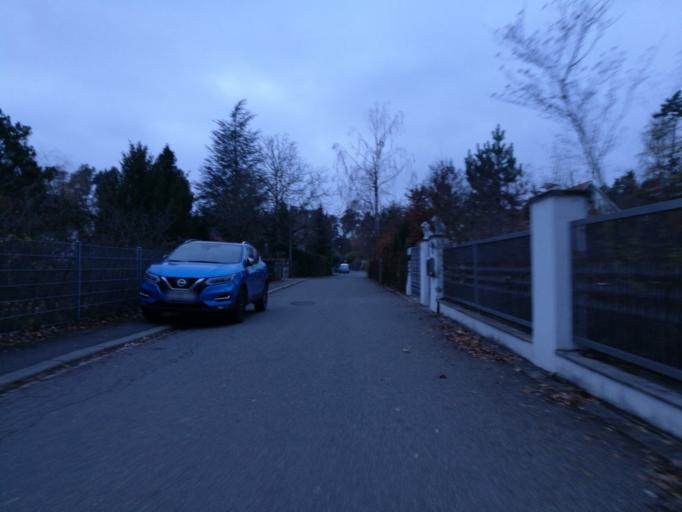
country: DE
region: Bavaria
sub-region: Regierungsbezirk Mittelfranken
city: Seukendorf
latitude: 49.4704
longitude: 10.8857
